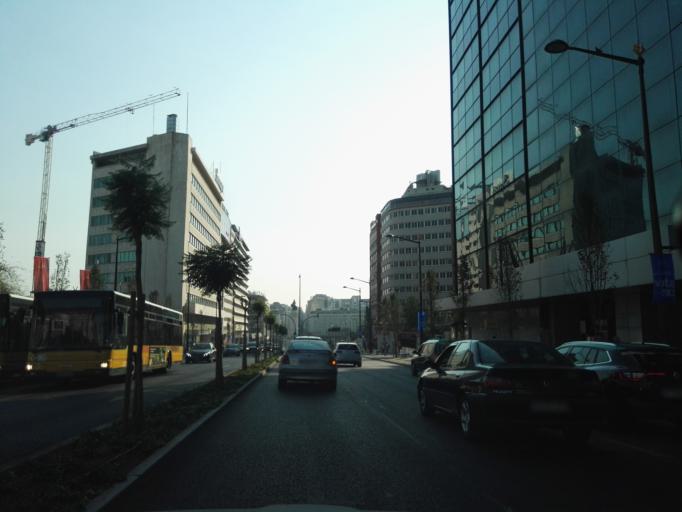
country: PT
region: Lisbon
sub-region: Lisbon
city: Lisbon
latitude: 38.7290
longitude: -9.1479
